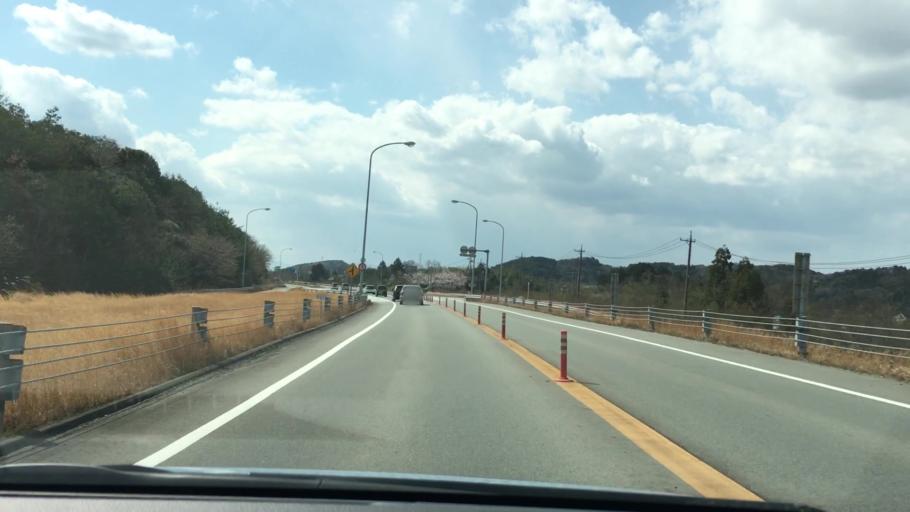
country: JP
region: Mie
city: Toba
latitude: 34.4944
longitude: 136.7799
